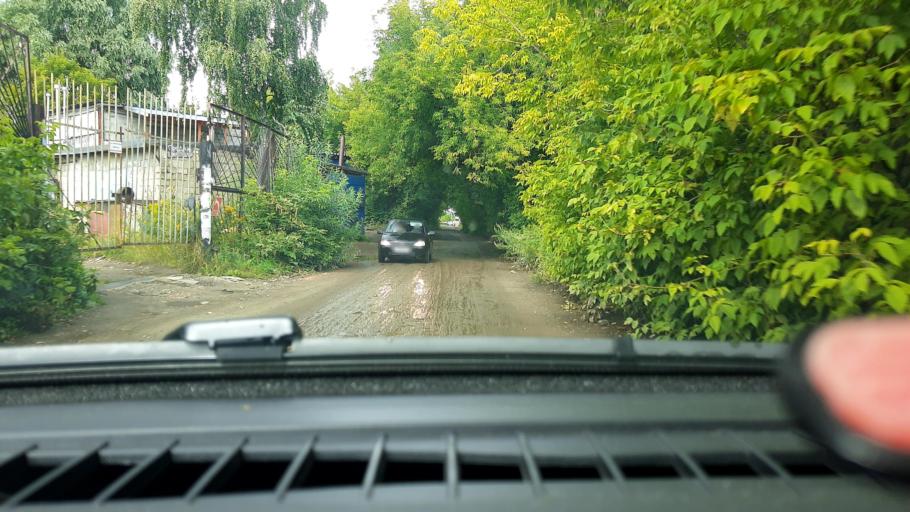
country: RU
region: Nizjnij Novgorod
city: Gorbatovka
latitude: 56.2554
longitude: 43.8318
